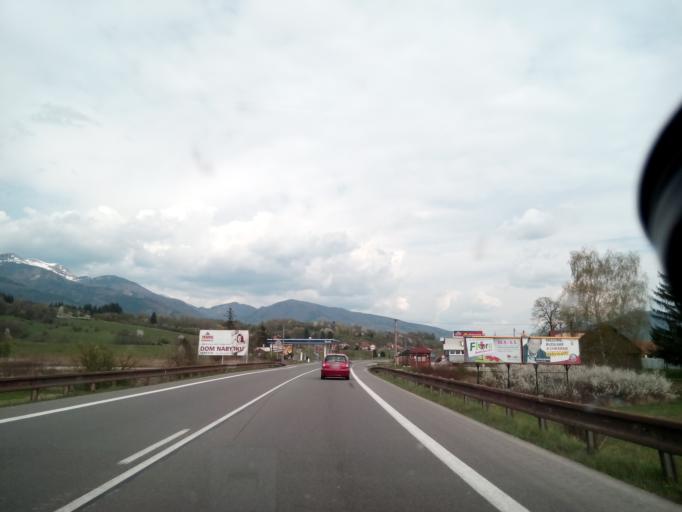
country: SK
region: Zilinsky
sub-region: Okres Zilina
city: Vrutky
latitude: 49.1163
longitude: 19.0261
